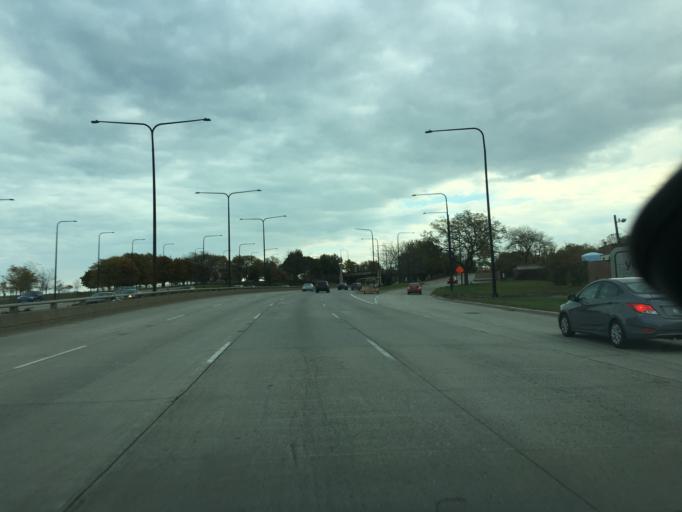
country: US
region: Illinois
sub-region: Cook County
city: Chicago
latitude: 41.8275
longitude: -87.6024
